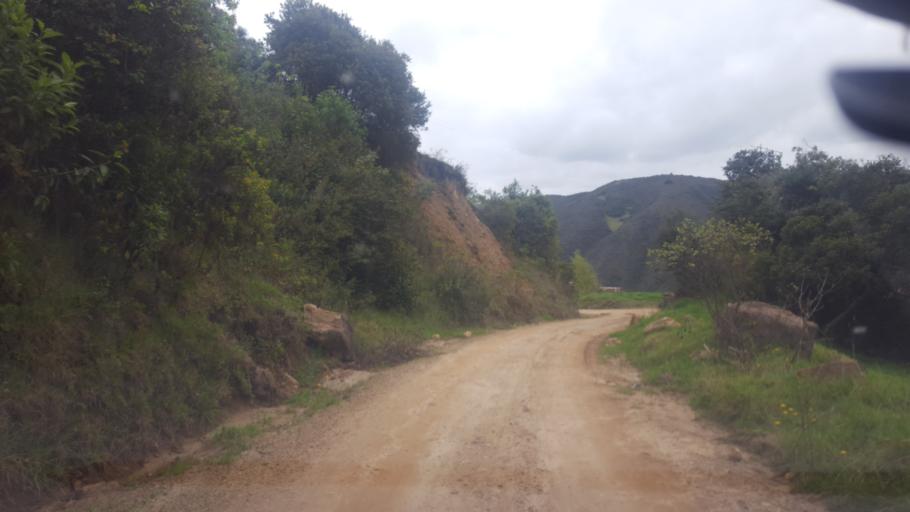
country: CO
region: Boyaca
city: Belen
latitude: 6.0223
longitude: -72.8801
